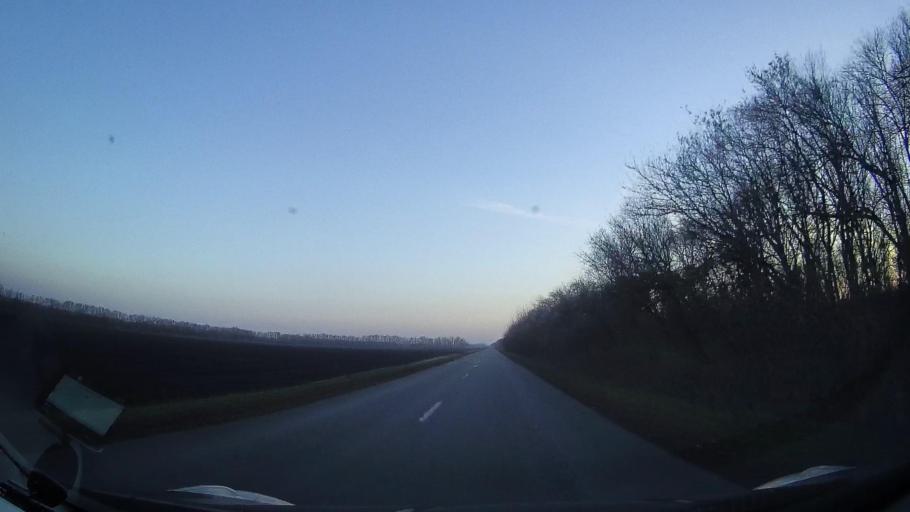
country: RU
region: Rostov
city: Zernograd
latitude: 47.0166
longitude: 40.3916
